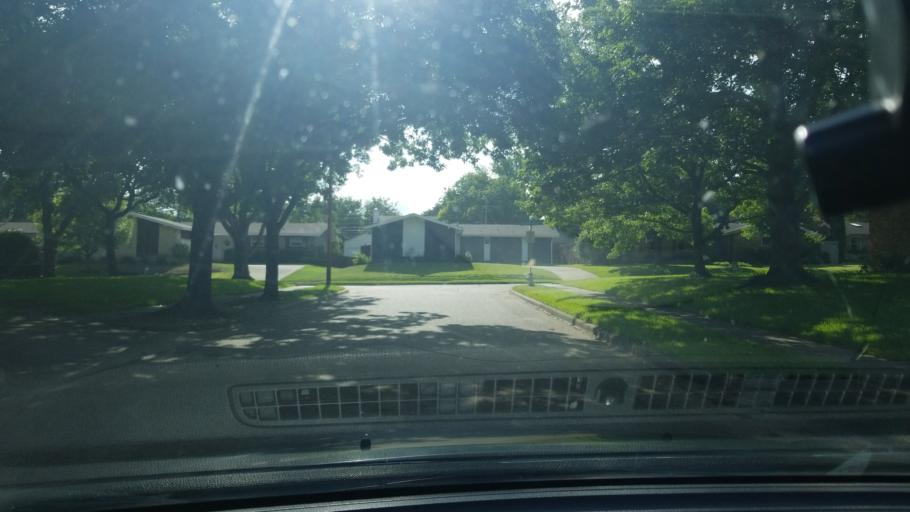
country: US
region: Texas
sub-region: Dallas County
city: Highland Park
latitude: 32.8209
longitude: -96.6890
